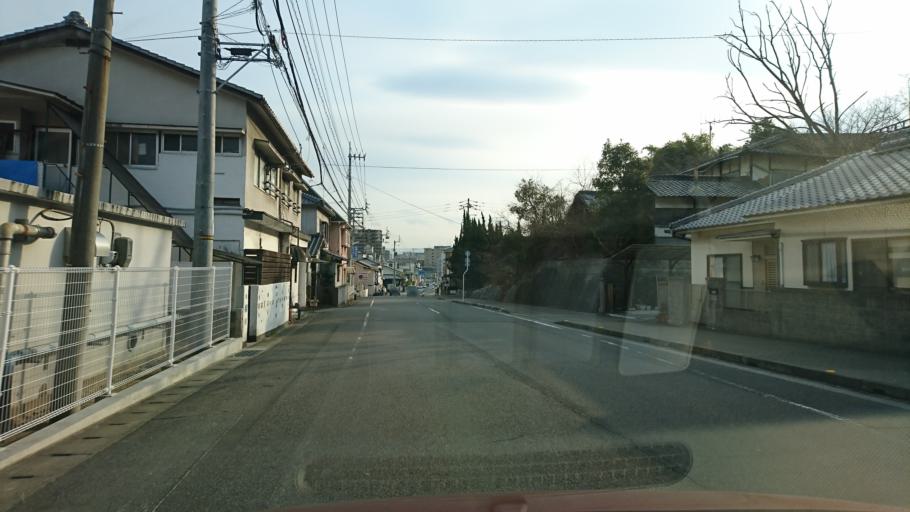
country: JP
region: Ehime
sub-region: Shikoku-chuo Shi
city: Matsuyama
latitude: 33.8557
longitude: 132.7761
